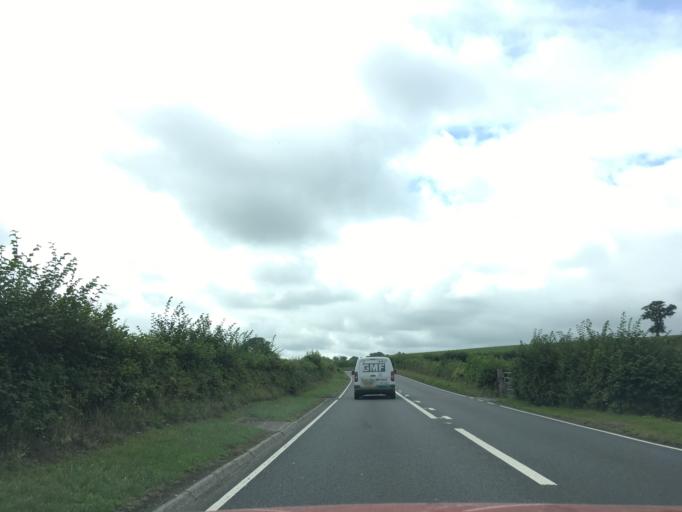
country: GB
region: Wales
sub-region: Carmarthenshire
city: Llanddarog
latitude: 51.8728
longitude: -4.1367
